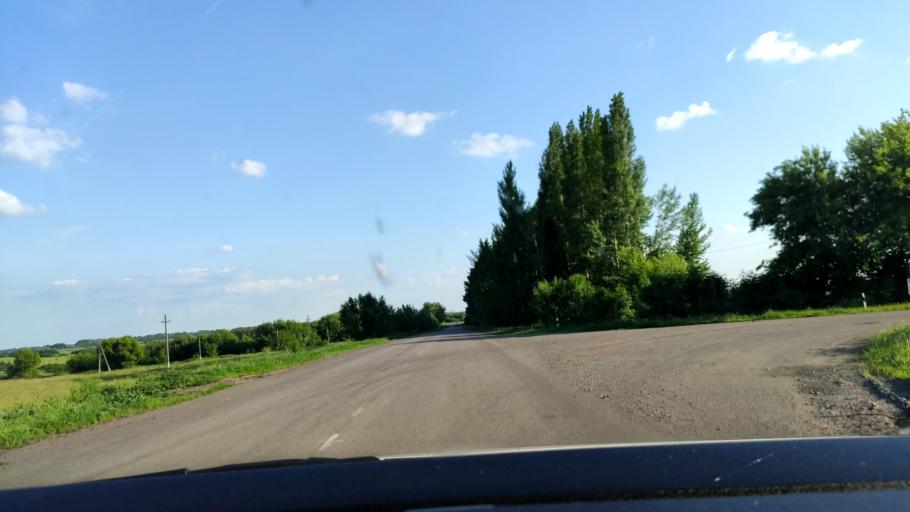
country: RU
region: Voronezj
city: Kashirskoye
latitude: 51.5112
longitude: 39.8326
